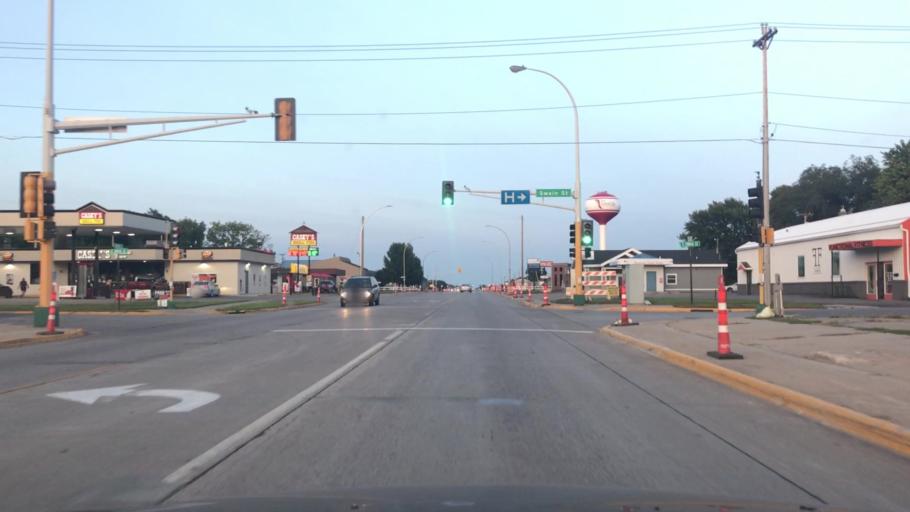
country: US
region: Minnesota
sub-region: Redwood County
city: Redwood Falls
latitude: 44.5414
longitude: -95.1102
